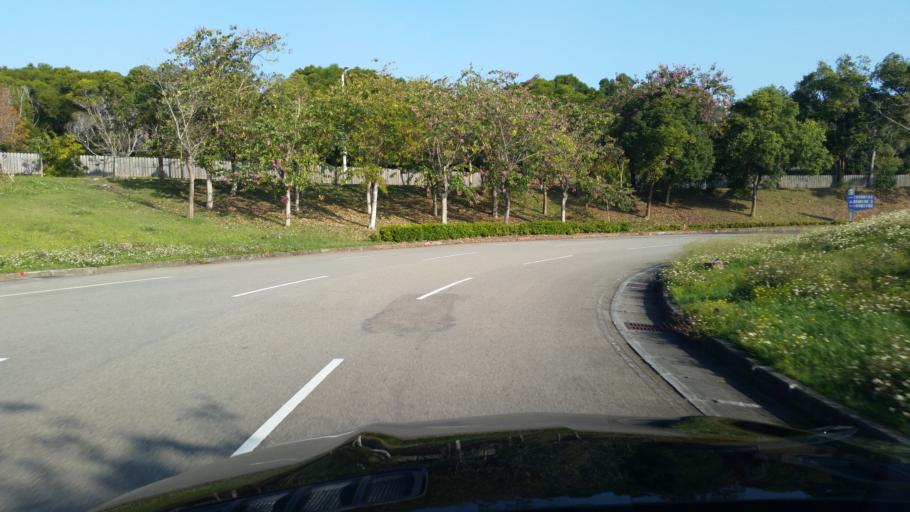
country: TW
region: Taiwan
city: Fengyuan
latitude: 24.3189
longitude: 120.6919
